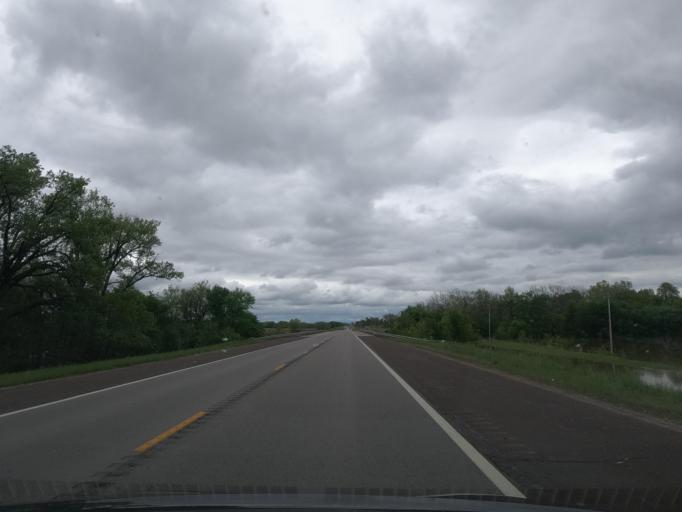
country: US
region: Kansas
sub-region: Labette County
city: Parsons
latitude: 37.3403
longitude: -95.1070
